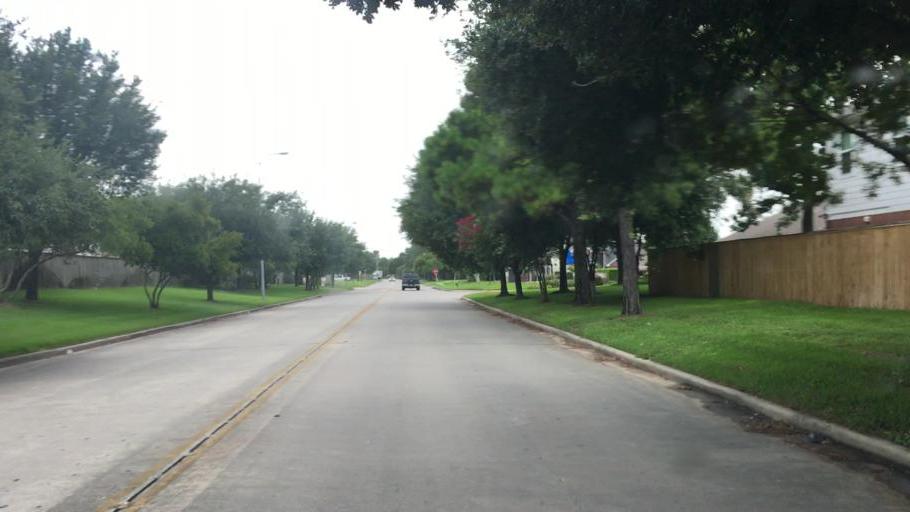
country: US
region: Texas
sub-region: Harris County
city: Atascocita
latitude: 29.9847
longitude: -95.1638
